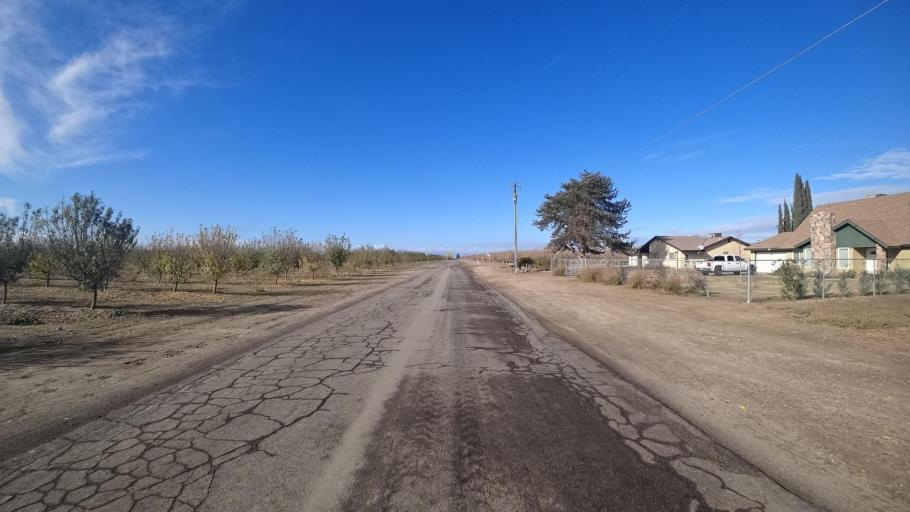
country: US
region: California
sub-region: Kern County
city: Rosedale
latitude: 35.3835
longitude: -119.2568
